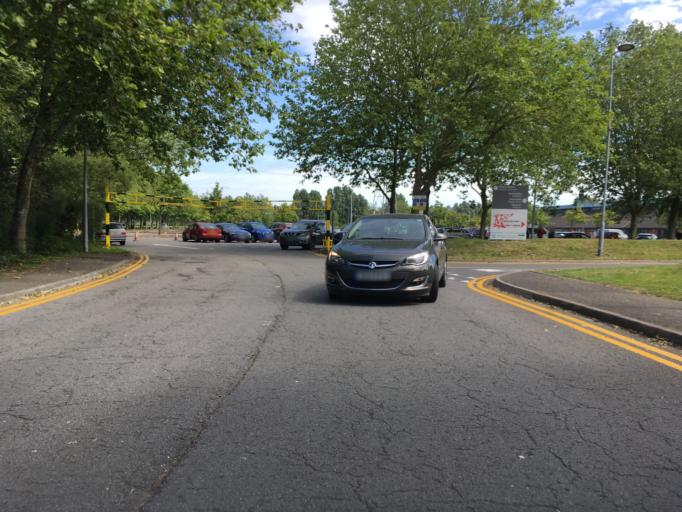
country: GB
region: Wales
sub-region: Newport
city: Nash
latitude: 51.5729
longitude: -2.9620
